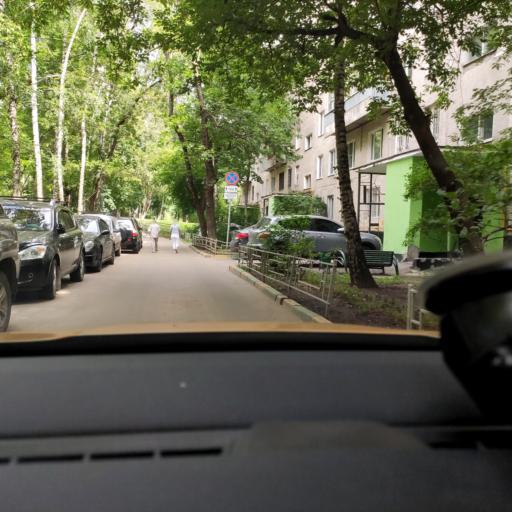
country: RU
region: Moscow
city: Tsaritsyno
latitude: 55.6166
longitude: 37.6491
